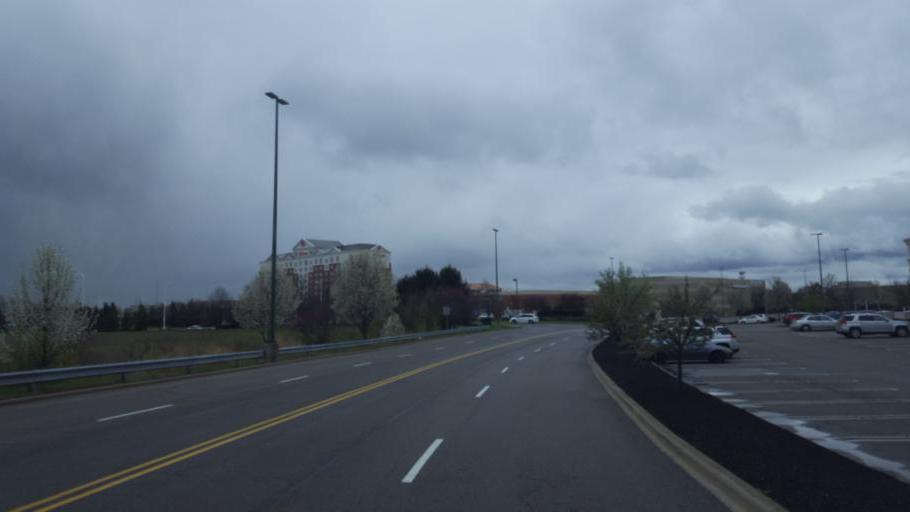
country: US
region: Ohio
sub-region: Franklin County
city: Westerville
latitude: 40.1461
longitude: -82.9769
